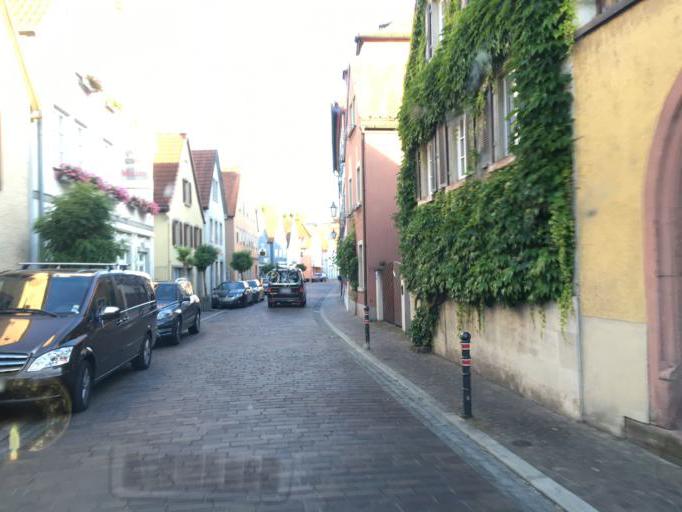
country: DE
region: Bavaria
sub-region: Regierungsbezirk Unterfranken
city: Margetshochheim
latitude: 49.8338
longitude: 9.8723
